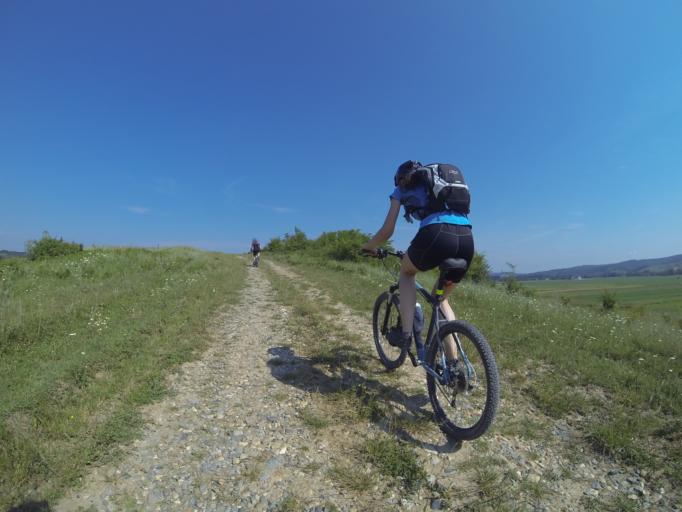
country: RO
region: Gorj
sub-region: Comuna Crusetu
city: Crusetu
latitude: 44.6060
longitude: 23.6802
